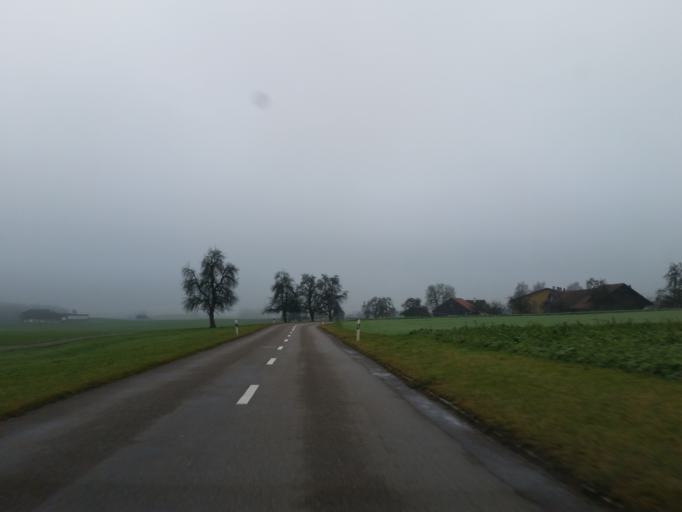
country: CH
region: Saint Gallen
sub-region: Wahlkreis Wil
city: Niederhelfenschwil
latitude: 47.4917
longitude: 9.1765
